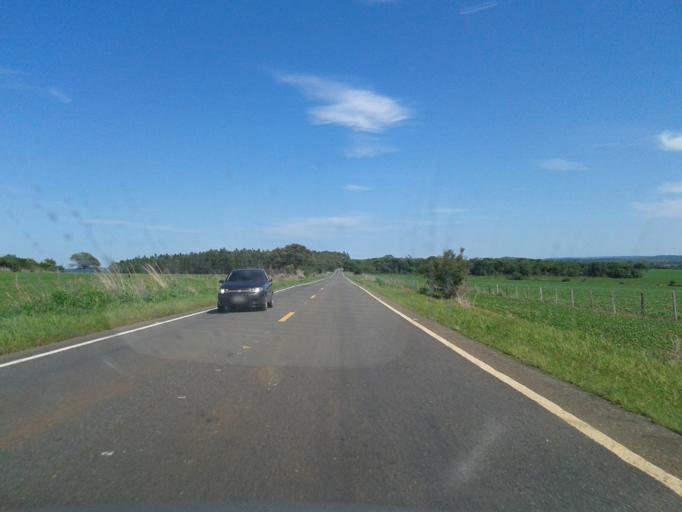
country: BR
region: Goias
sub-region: Piracanjuba
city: Piracanjuba
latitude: -17.3364
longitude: -48.7960
